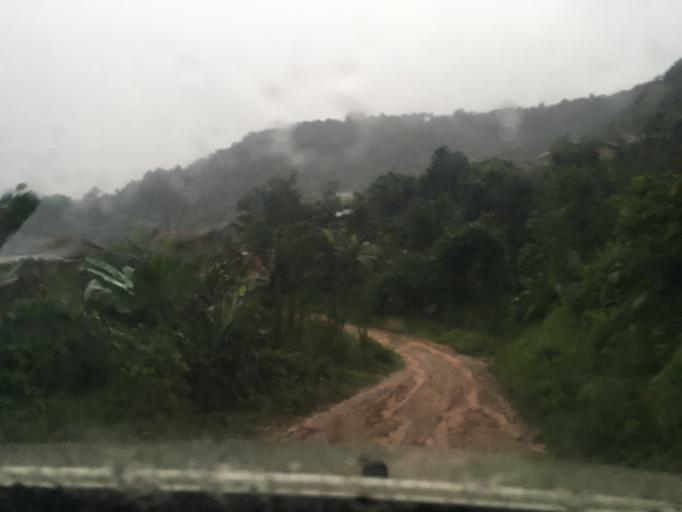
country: LA
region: Oudomxai
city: Muang La
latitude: 21.2390
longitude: 101.9553
